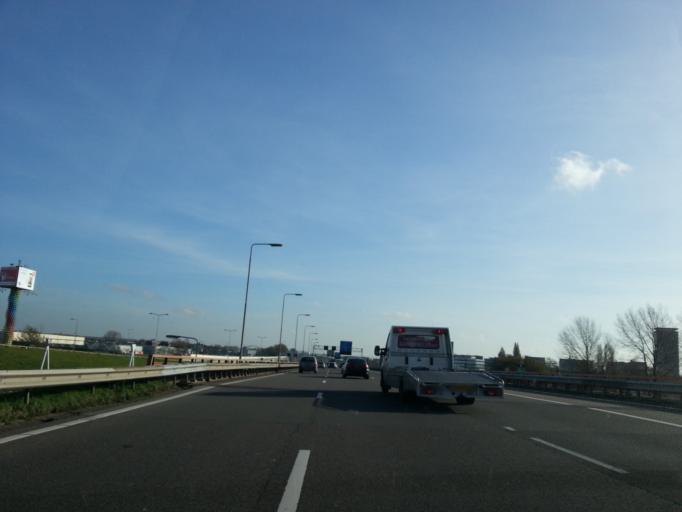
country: NL
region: South Holland
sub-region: Gemeente Den Haag
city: Ypenburg
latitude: 52.0600
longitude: 4.3800
